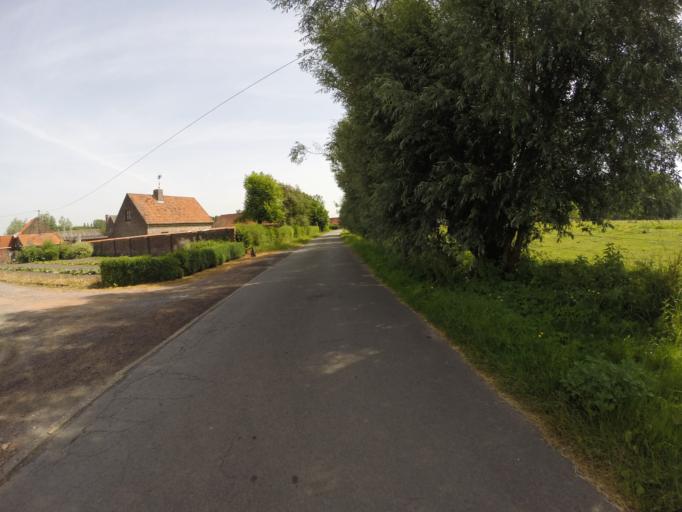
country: BE
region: Flanders
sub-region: Provincie Oost-Vlaanderen
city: Nevele
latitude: 51.0680
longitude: 3.5443
